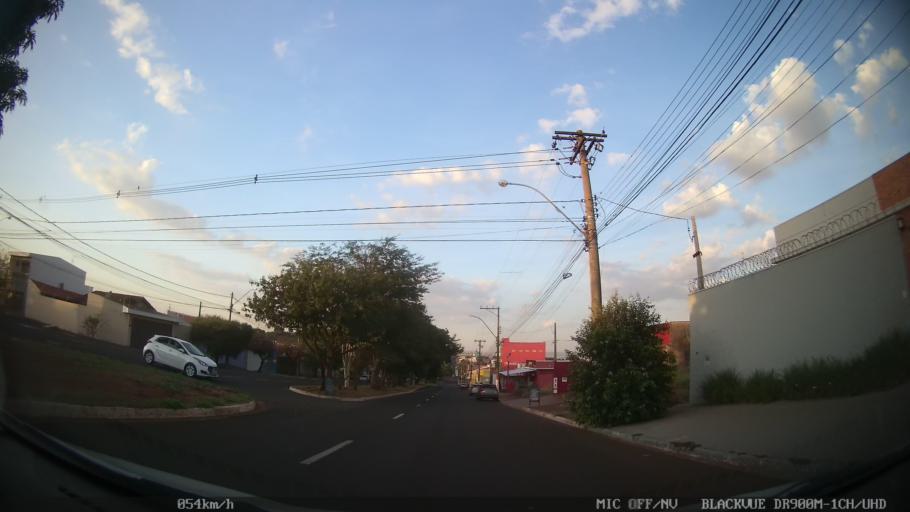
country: BR
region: Sao Paulo
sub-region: Ribeirao Preto
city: Ribeirao Preto
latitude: -21.1407
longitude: -47.8544
